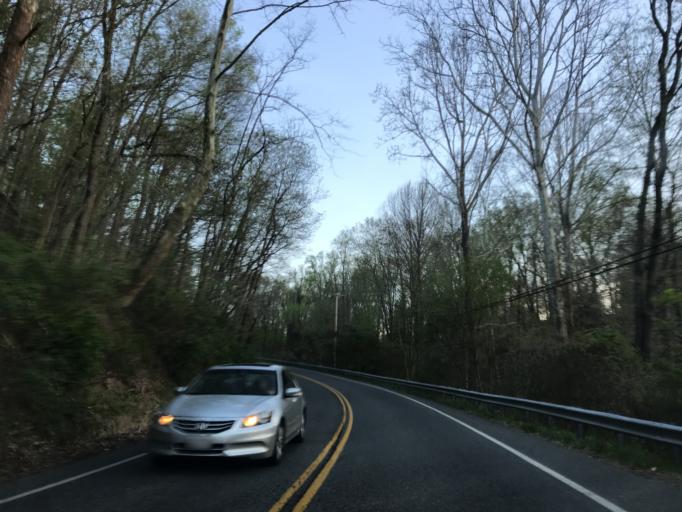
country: US
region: Maryland
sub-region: Harford County
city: Fallston
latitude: 39.5504
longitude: -76.4363
